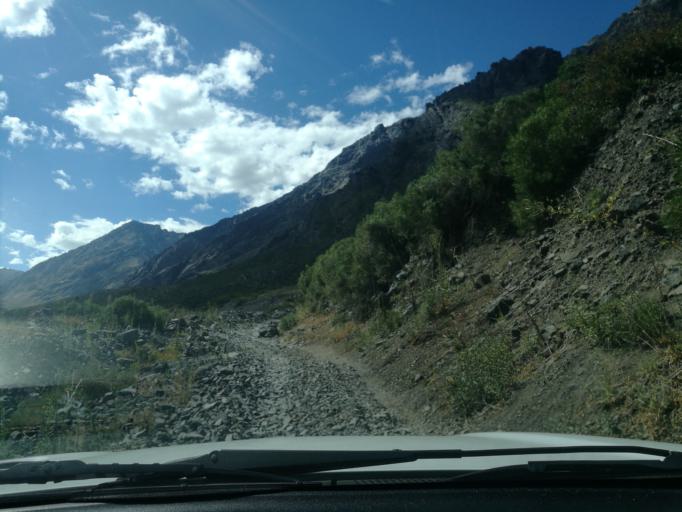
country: CL
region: O'Higgins
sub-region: Provincia de Cachapoal
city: Machali
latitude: -34.3941
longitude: -70.2738
